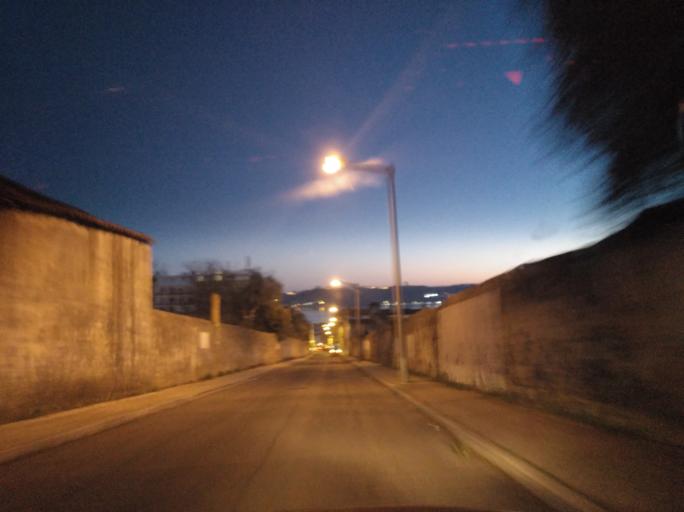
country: PT
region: Lisbon
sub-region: Oeiras
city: Alges
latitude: 38.7066
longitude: -9.1965
